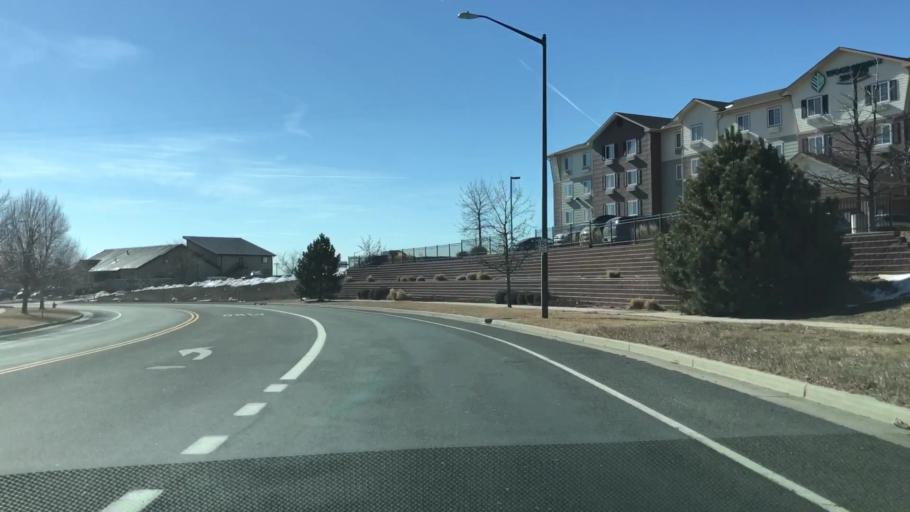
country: US
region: Colorado
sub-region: Larimer County
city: Loveland
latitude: 40.4326
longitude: -104.9904
